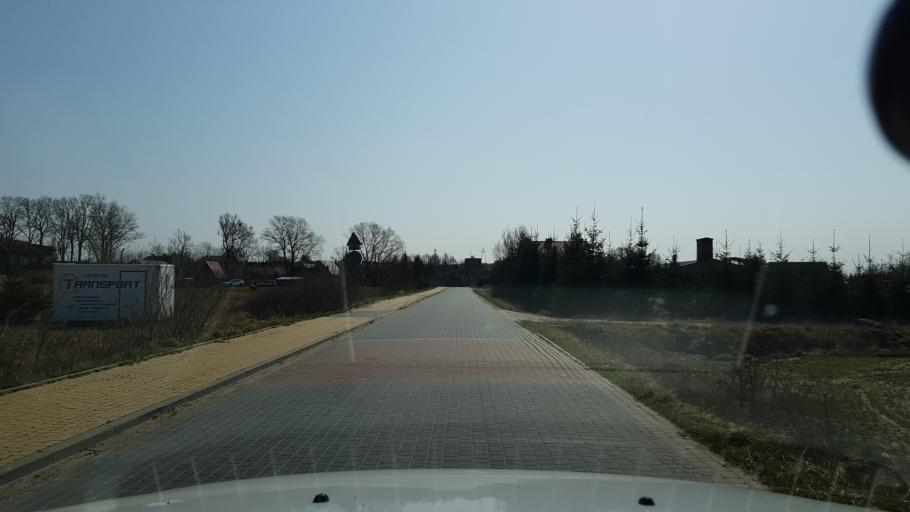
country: PL
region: West Pomeranian Voivodeship
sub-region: Powiat slawienski
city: Darlowo
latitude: 54.5098
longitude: 16.5014
